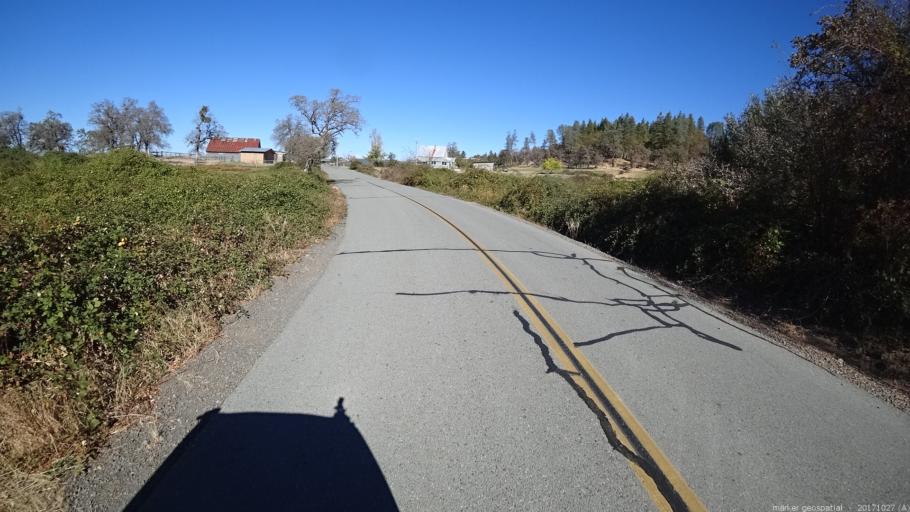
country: US
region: California
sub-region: Shasta County
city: Shingletown
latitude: 40.7586
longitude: -121.9672
